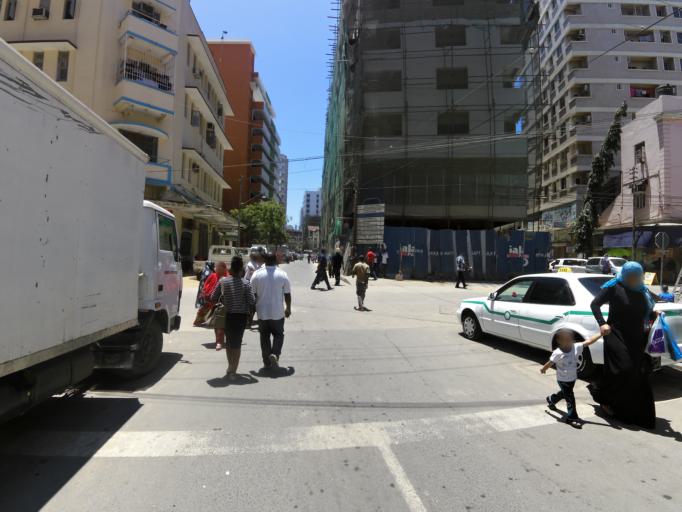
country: TZ
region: Dar es Salaam
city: Dar es Salaam
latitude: -6.8192
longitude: 39.2853
